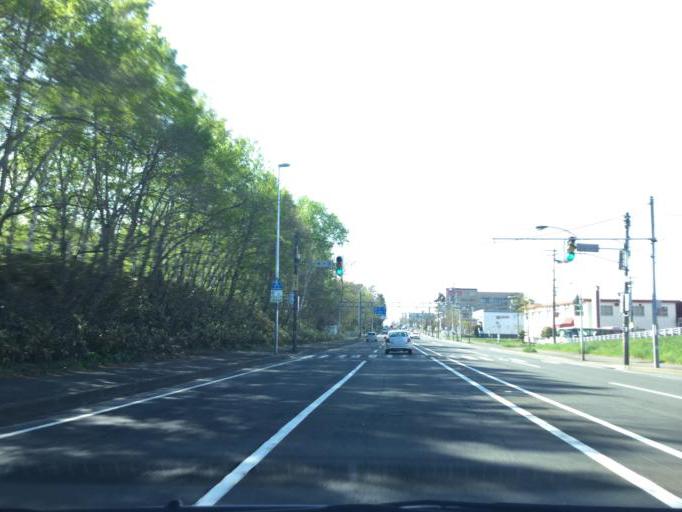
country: JP
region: Hokkaido
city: Sapporo
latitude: 43.0087
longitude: 141.4253
